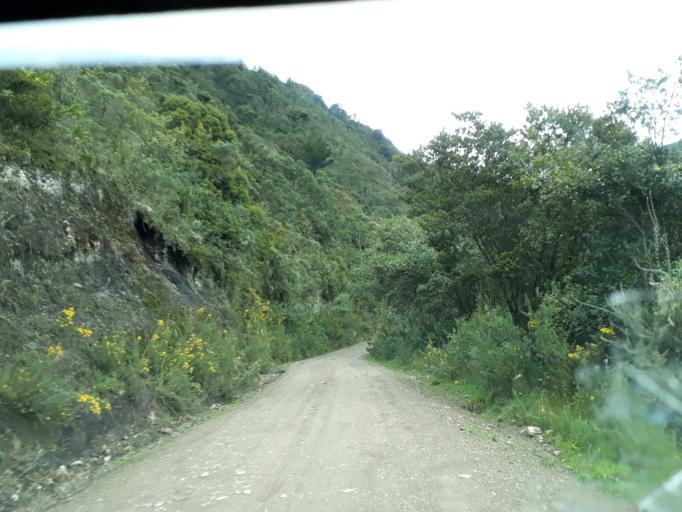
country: CO
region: Cundinamarca
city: Cogua
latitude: 5.1590
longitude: -73.9868
